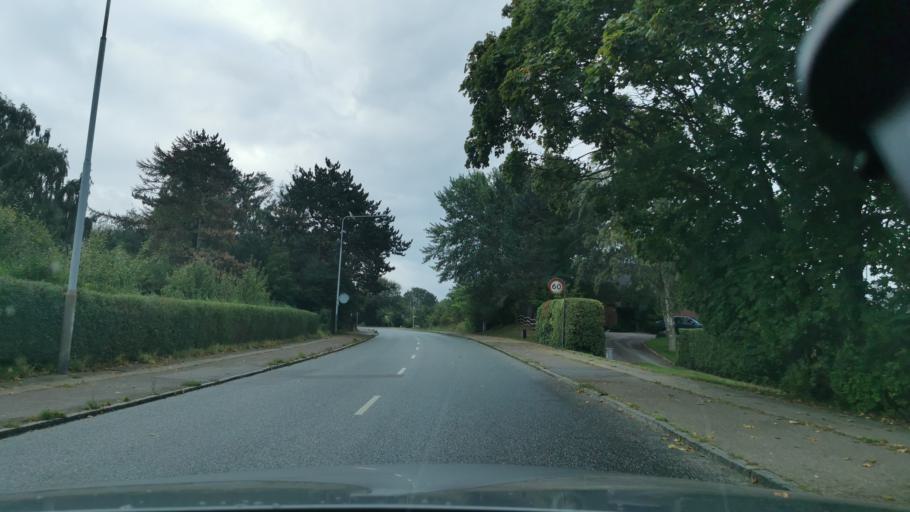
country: DK
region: Zealand
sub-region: Kalundborg Kommune
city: Kalundborg
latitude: 55.7037
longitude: 11.0244
